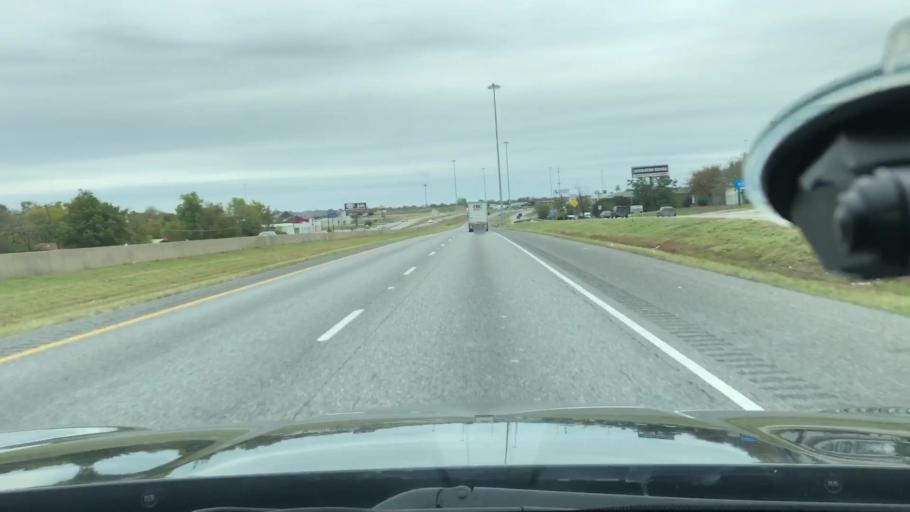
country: US
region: Texas
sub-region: Hunt County
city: Greenville
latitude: 33.1090
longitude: -96.1021
